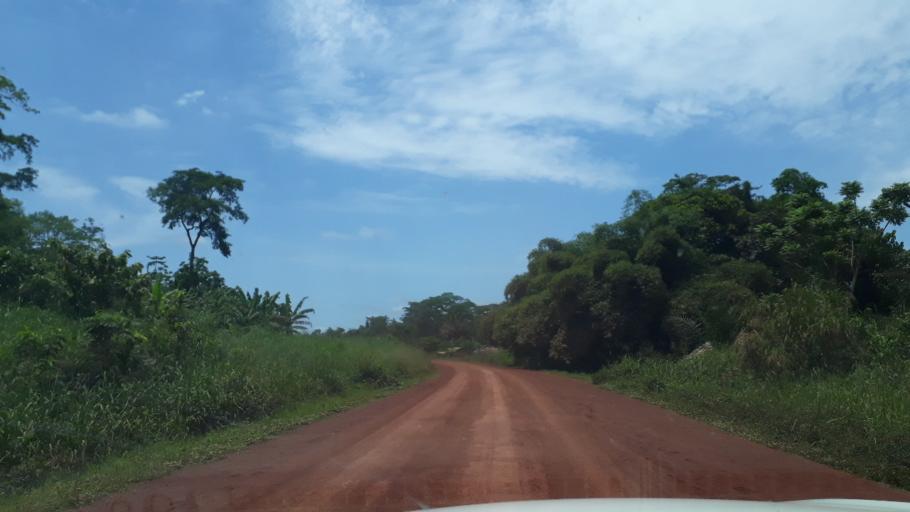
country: CD
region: Eastern Province
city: Kisangani
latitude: 0.4679
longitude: 25.5262
